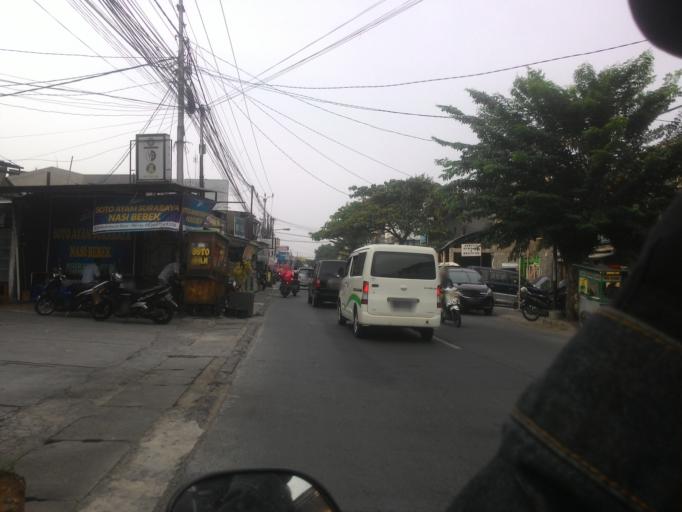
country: ID
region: West Java
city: Depok
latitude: -6.3996
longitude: 106.8362
